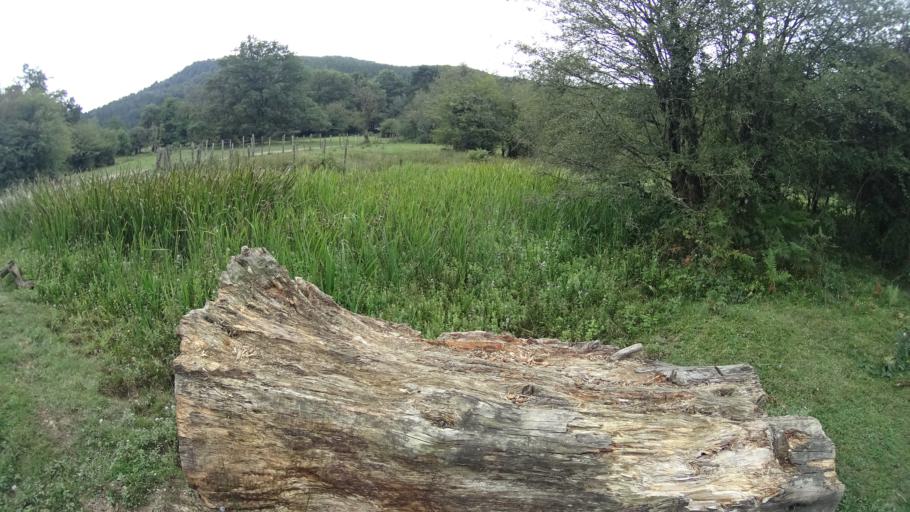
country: ES
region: Basque Country
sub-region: Bizkaia
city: Zeanuri
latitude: 43.0499
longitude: -2.7212
